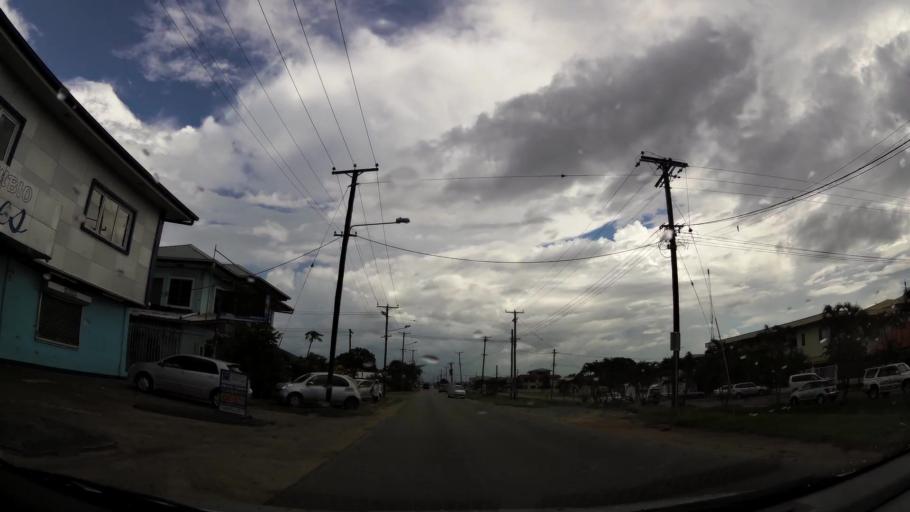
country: SR
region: Paramaribo
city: Paramaribo
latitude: 5.8516
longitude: -55.1331
